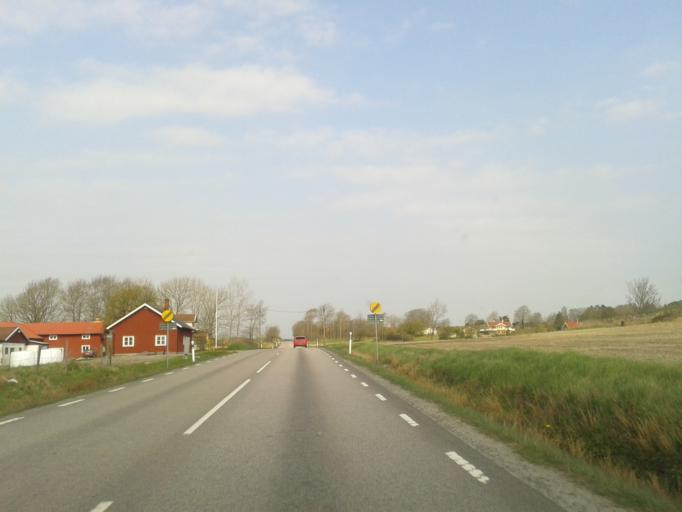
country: SE
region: Vaestra Goetaland
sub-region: Kungalvs Kommun
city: Kungalv
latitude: 57.8723
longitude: 11.9084
